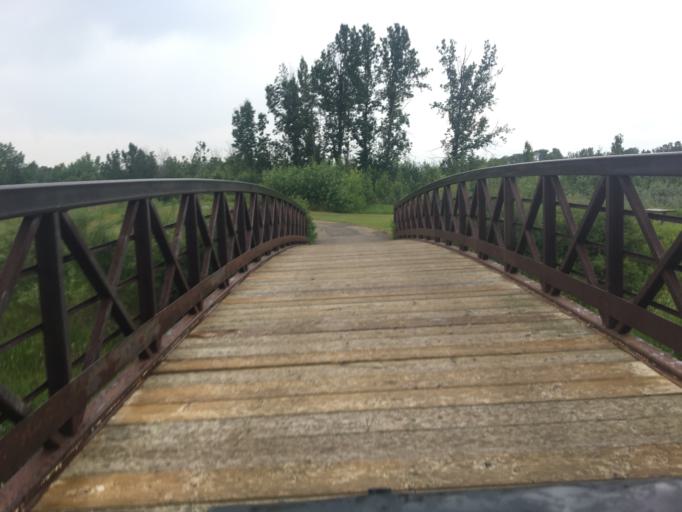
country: CA
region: Alberta
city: Grande Prairie
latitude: 55.1514
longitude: -118.8019
